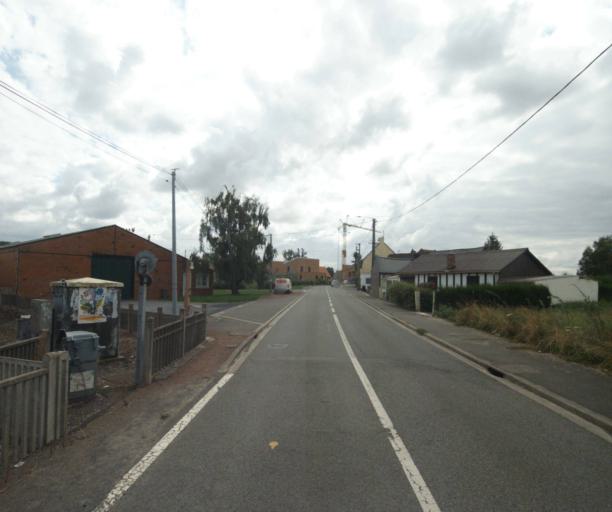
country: FR
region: Nord-Pas-de-Calais
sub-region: Departement du Nord
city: Anstaing
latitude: 50.6094
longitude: 3.1905
